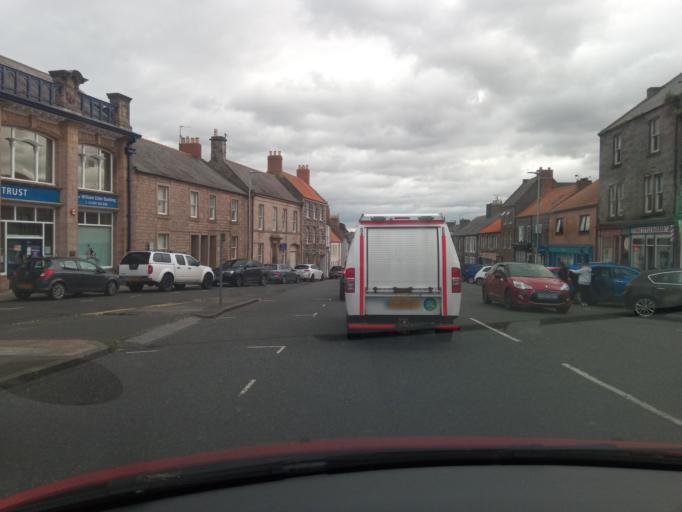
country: GB
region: England
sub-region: Northumberland
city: Berwick-Upon-Tweed
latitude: 55.7732
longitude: -2.0084
